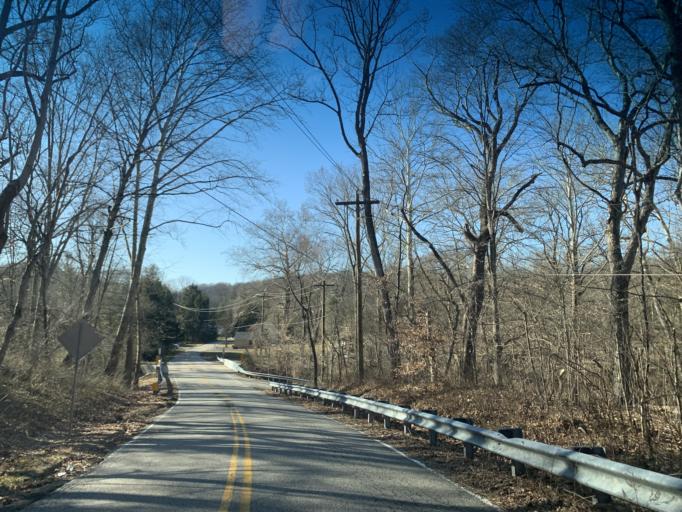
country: US
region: Maryland
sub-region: Cecil County
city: Rising Sun
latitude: 39.6548
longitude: -76.1165
